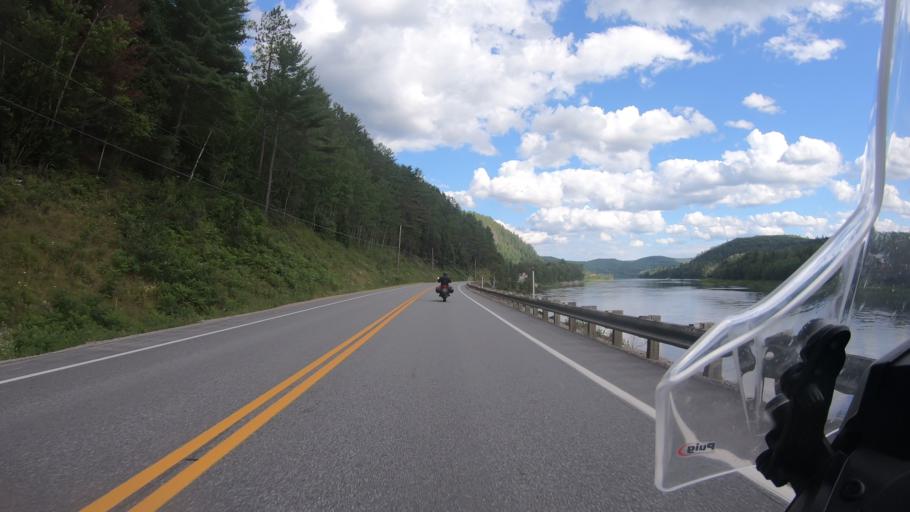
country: CA
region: Quebec
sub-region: Mauricie
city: Saint-Tite
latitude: 46.9961
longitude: -72.9195
